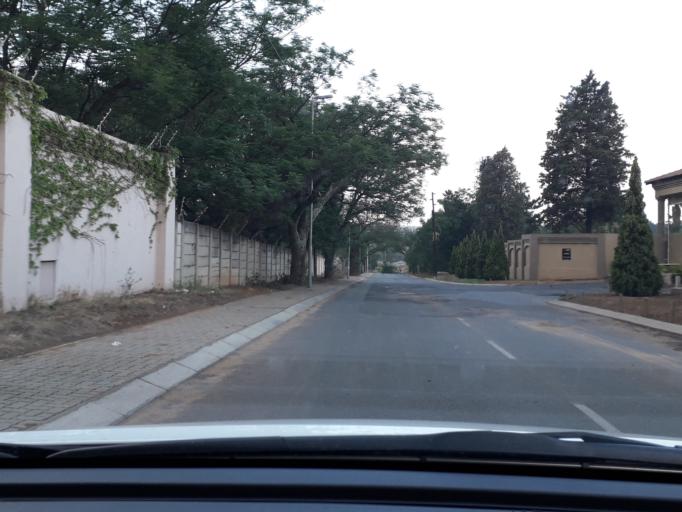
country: ZA
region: Gauteng
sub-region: City of Johannesburg Metropolitan Municipality
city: Diepsloot
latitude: -25.9953
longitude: 27.9945
